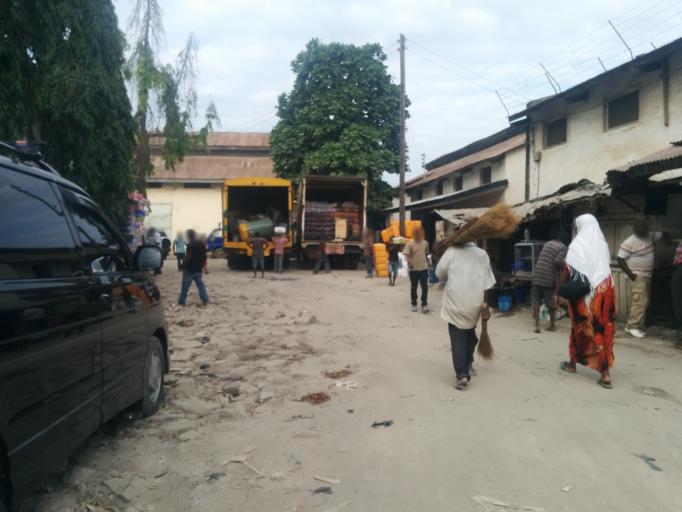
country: TZ
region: Dar es Salaam
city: Dar es Salaam
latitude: -6.8294
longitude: 39.2757
